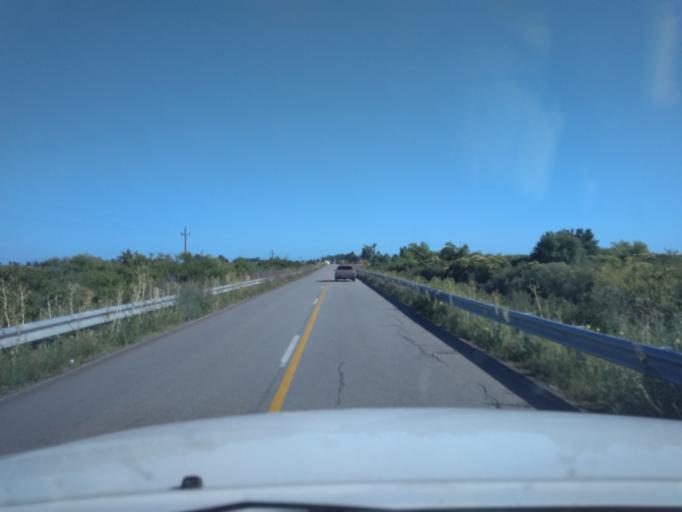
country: UY
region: Canelones
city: San Ramon
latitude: -34.3259
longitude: -55.9612
